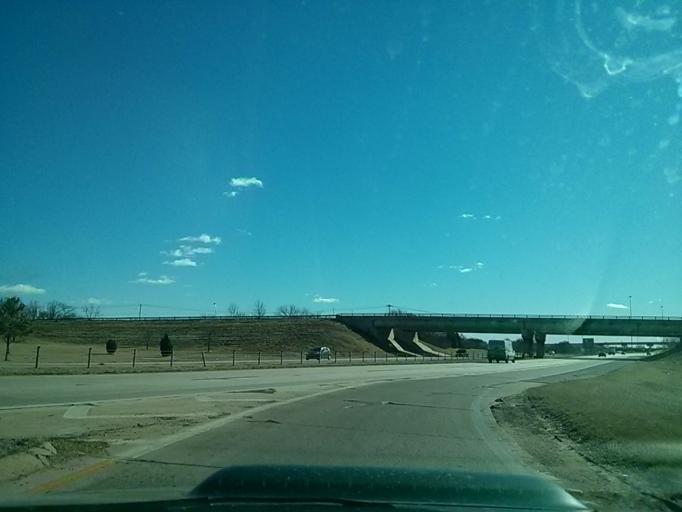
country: US
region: Oklahoma
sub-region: Tulsa County
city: Turley
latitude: 36.2075
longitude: -95.9467
